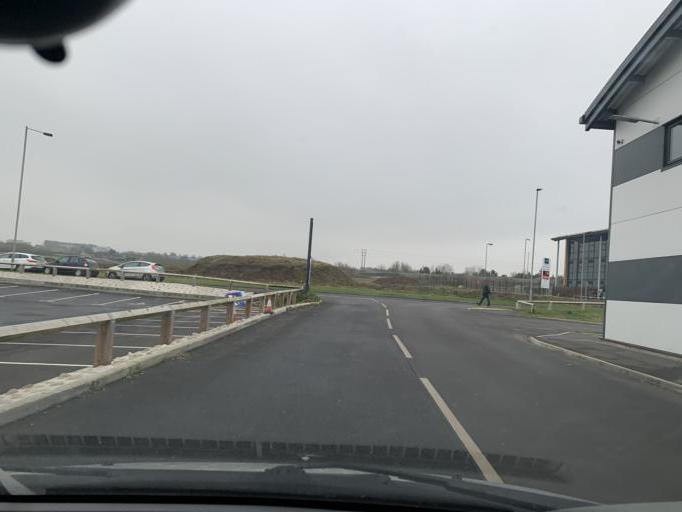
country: GB
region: England
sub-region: Wiltshire
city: Bulford
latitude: 51.1751
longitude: -1.7588
